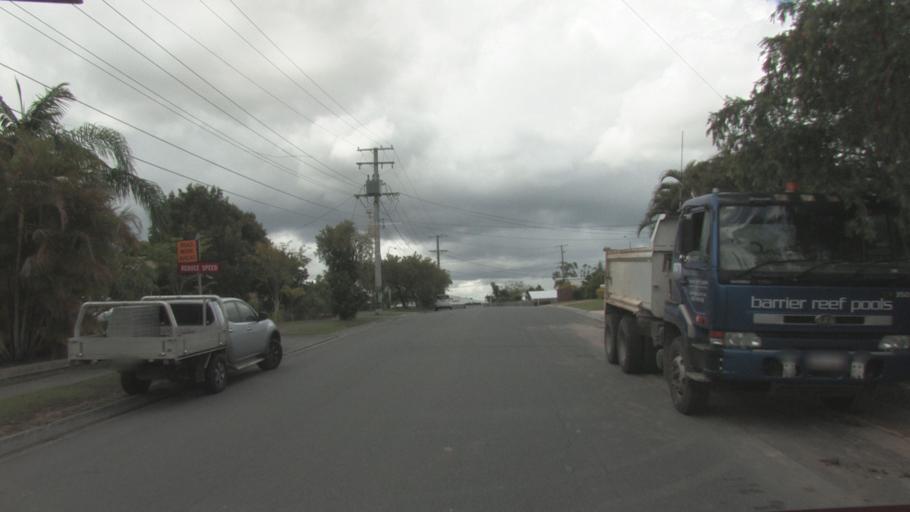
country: AU
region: Queensland
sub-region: Logan
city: Slacks Creek
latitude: -27.6498
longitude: 153.1653
